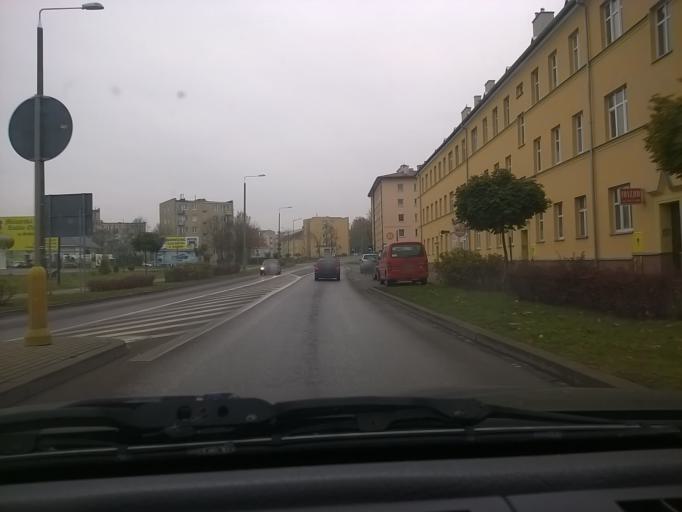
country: PL
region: Warmian-Masurian Voivodeship
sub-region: Powiat ketrzynski
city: Ketrzyn
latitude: 54.0817
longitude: 21.3593
